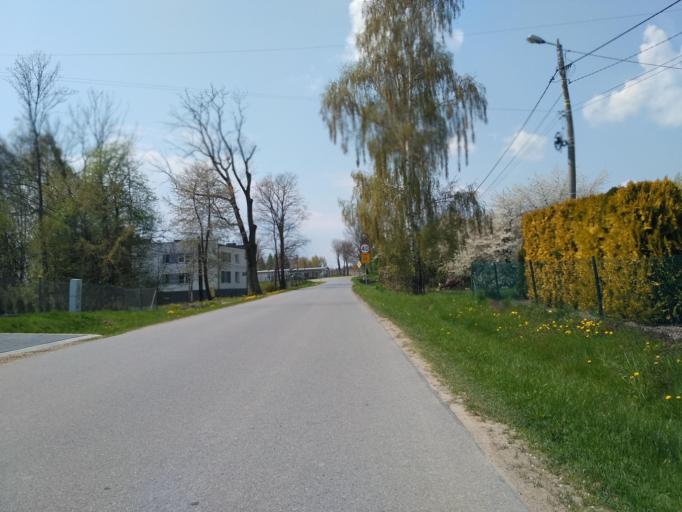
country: PL
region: Subcarpathian Voivodeship
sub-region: Powiat jasielski
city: Osiek Jasielski
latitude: 49.6716
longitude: 21.5399
